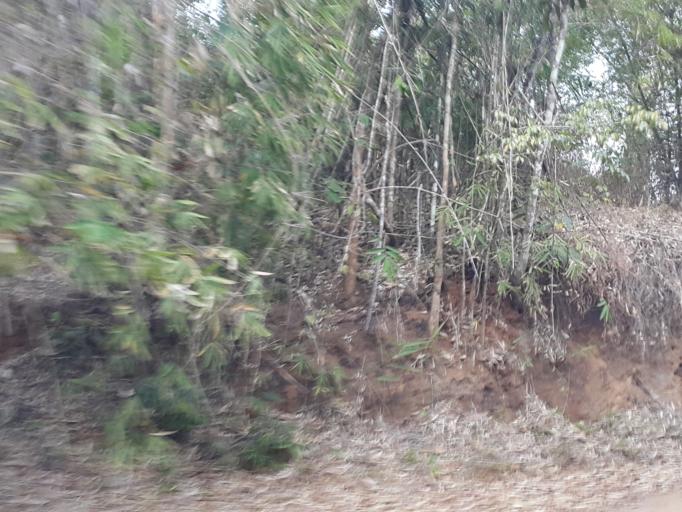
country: TH
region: Chiang Mai
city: Mae Taeng
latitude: 19.0581
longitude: 98.7688
